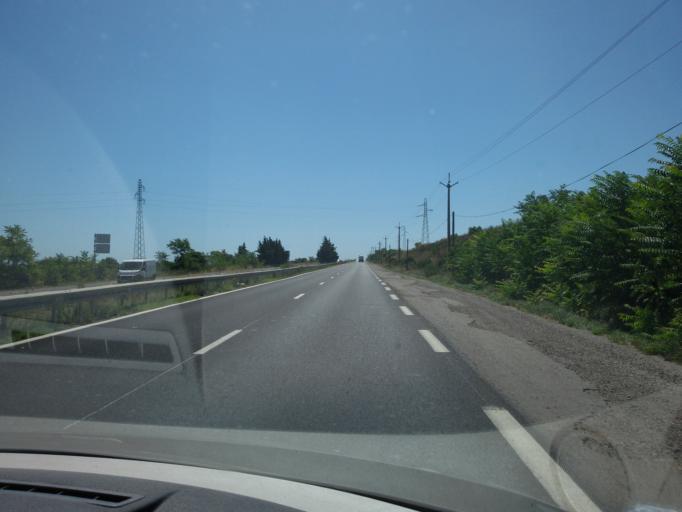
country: FR
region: Languedoc-Roussillon
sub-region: Departement de l'Herault
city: Saint-Jean-de-Vedas
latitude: 43.5410
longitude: 3.8228
